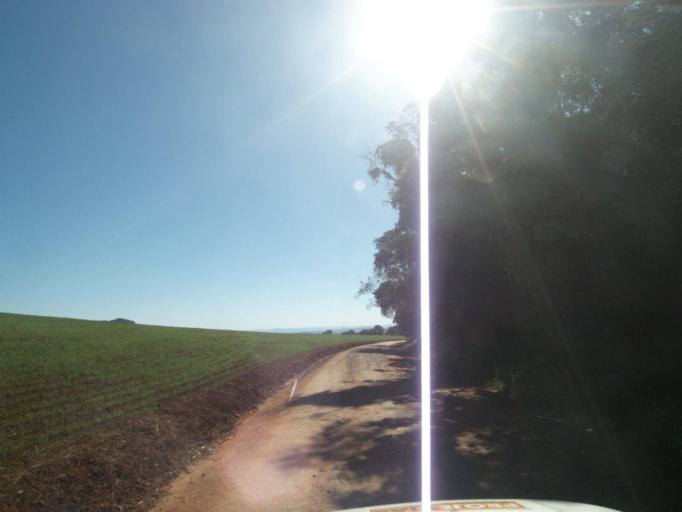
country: BR
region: Parana
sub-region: Tibagi
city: Tibagi
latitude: -24.5690
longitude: -50.6270
